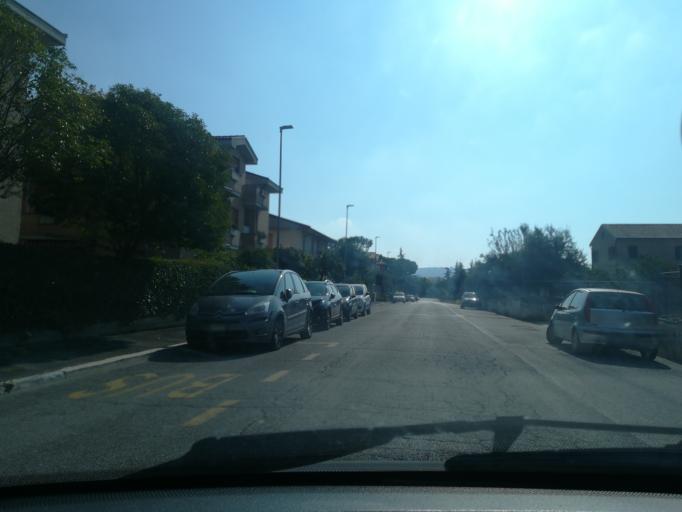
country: IT
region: The Marches
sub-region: Provincia di Macerata
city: Piediripa
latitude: 43.2758
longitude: 13.4754
